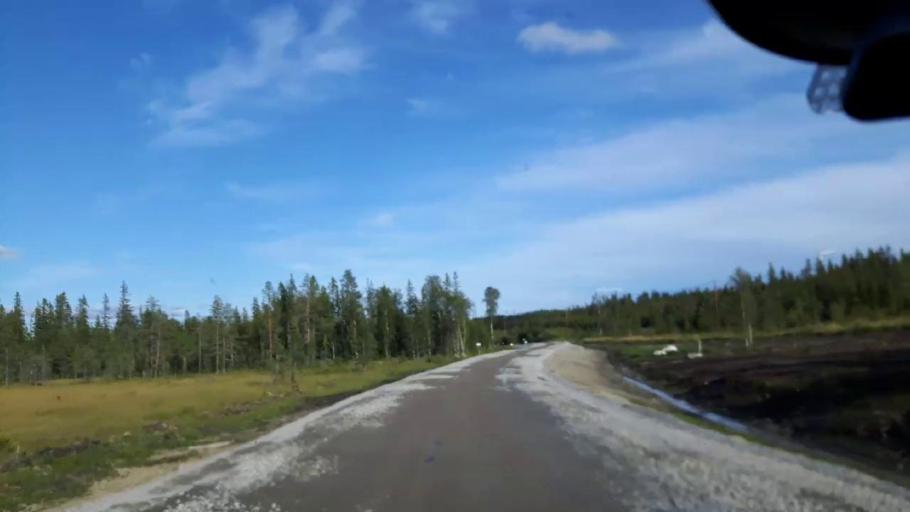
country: SE
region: Jaemtland
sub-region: Ragunda Kommun
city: Hammarstrand
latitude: 63.4260
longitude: 16.1467
